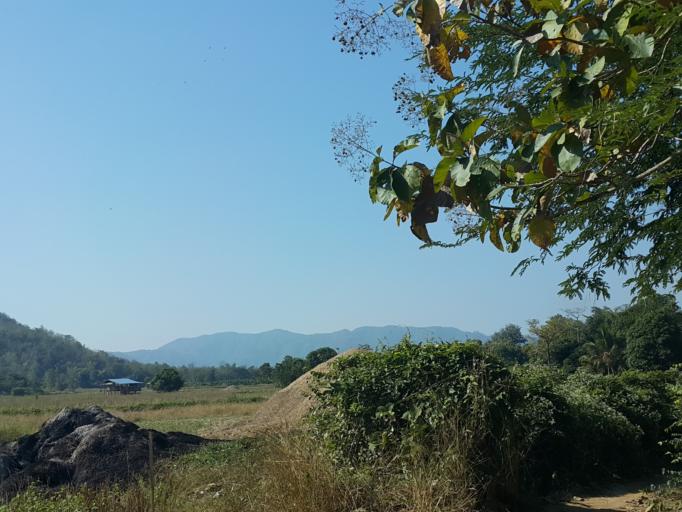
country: TH
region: Sukhothai
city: Thung Saliam
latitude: 17.3282
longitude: 99.4606
